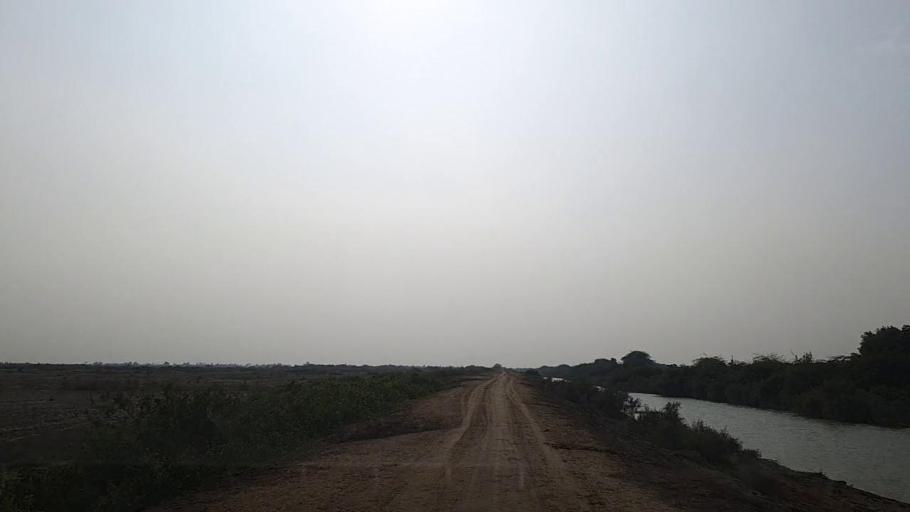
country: PK
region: Sindh
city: Gharo
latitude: 24.6641
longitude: 67.6314
